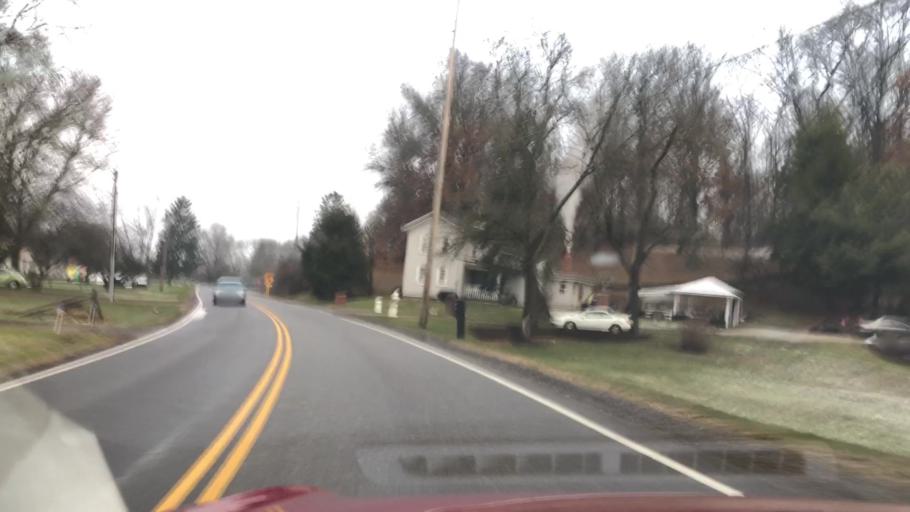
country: US
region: Ohio
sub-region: Stark County
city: Massillon
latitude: 40.8568
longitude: -81.5208
